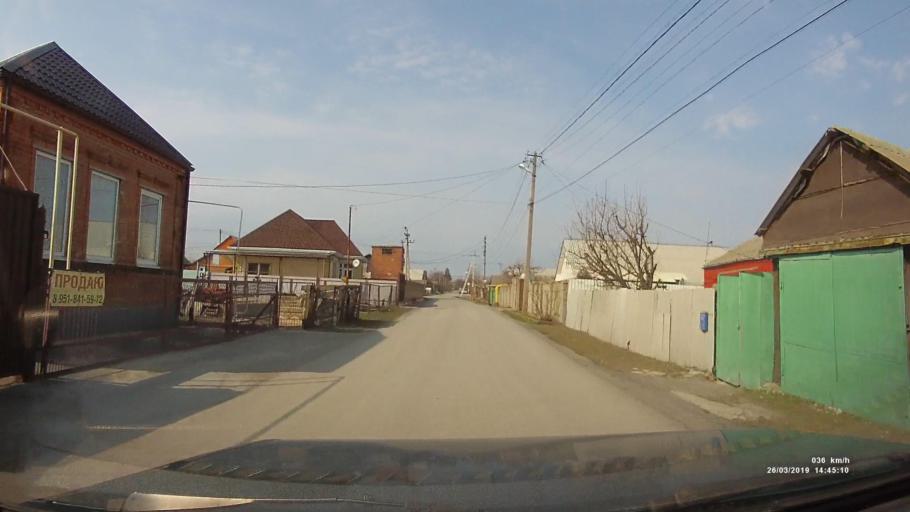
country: RU
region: Rostov
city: Novobessergenovka
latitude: 47.1813
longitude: 38.8620
